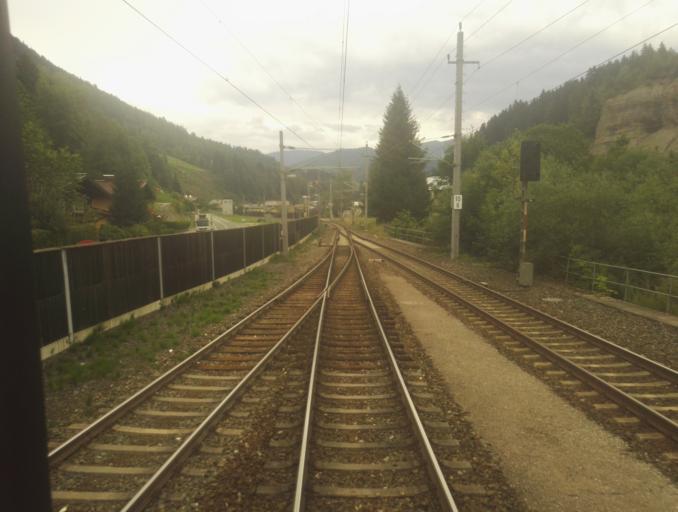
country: AT
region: Salzburg
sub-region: Politischer Bezirk Sankt Johann im Pongau
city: Huttau
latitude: 47.4185
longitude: 13.3262
